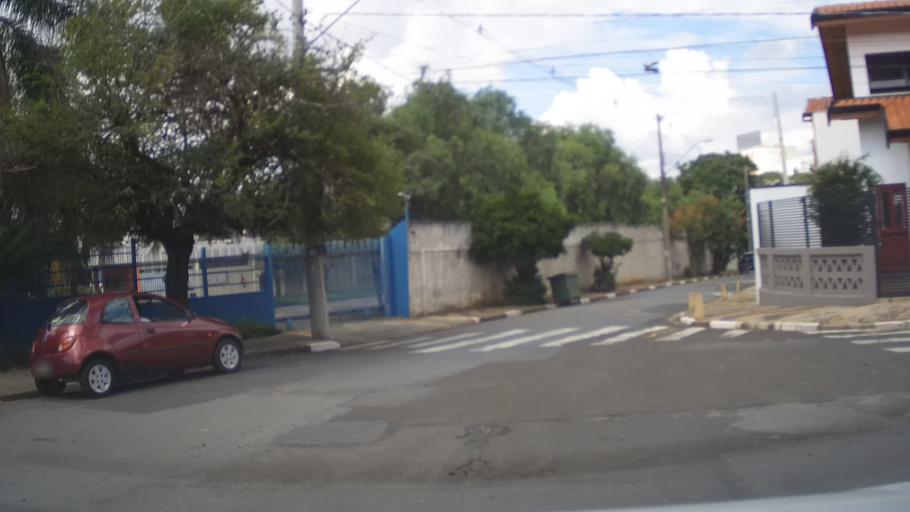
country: BR
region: Sao Paulo
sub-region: Campinas
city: Campinas
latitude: -22.8883
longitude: -47.0467
